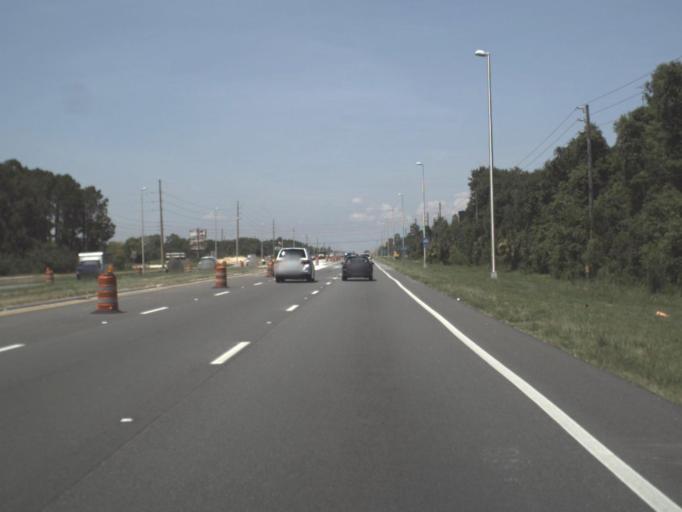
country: US
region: Florida
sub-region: Hernando County
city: Hernando Beach
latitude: 28.4132
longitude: -82.6498
